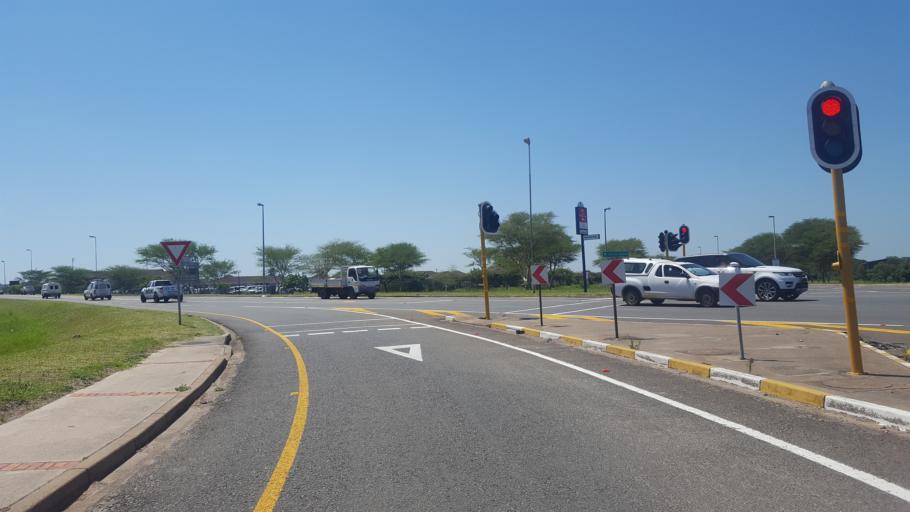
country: ZA
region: KwaZulu-Natal
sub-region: uThungulu District Municipality
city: Richards Bay
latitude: -28.7508
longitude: 32.0552
